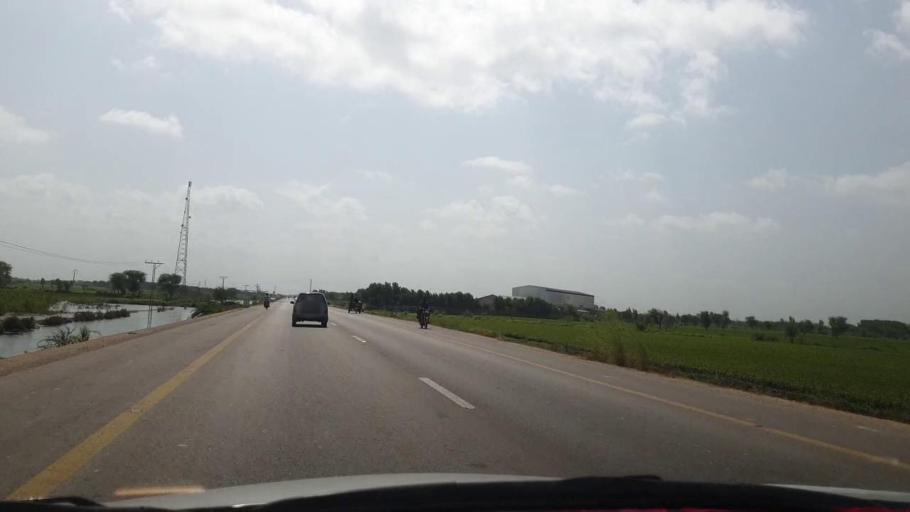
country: PK
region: Sindh
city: Matli
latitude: 24.9376
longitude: 68.7068
